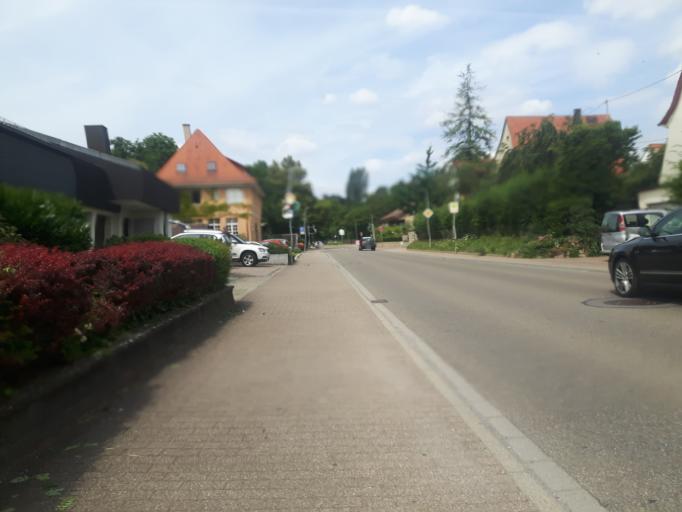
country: DE
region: Baden-Wuerttemberg
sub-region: Regierungsbezirk Stuttgart
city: Bonnigheim
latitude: 49.0404
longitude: 9.1018
